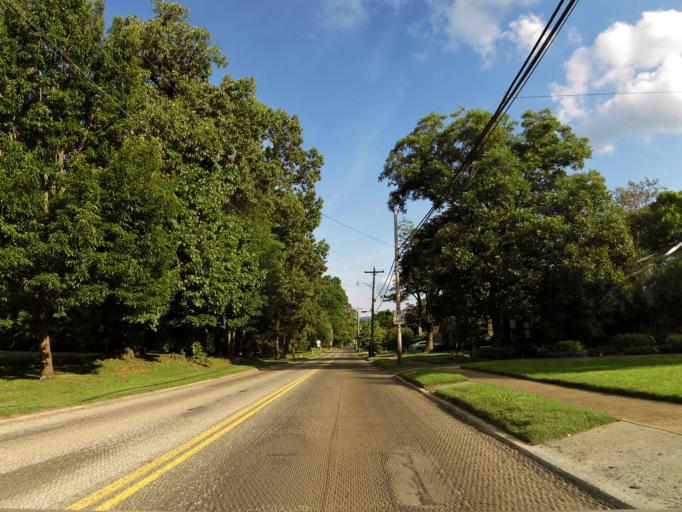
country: US
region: Tennessee
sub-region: Blount County
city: Maryville
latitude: 35.7488
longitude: -83.9651
